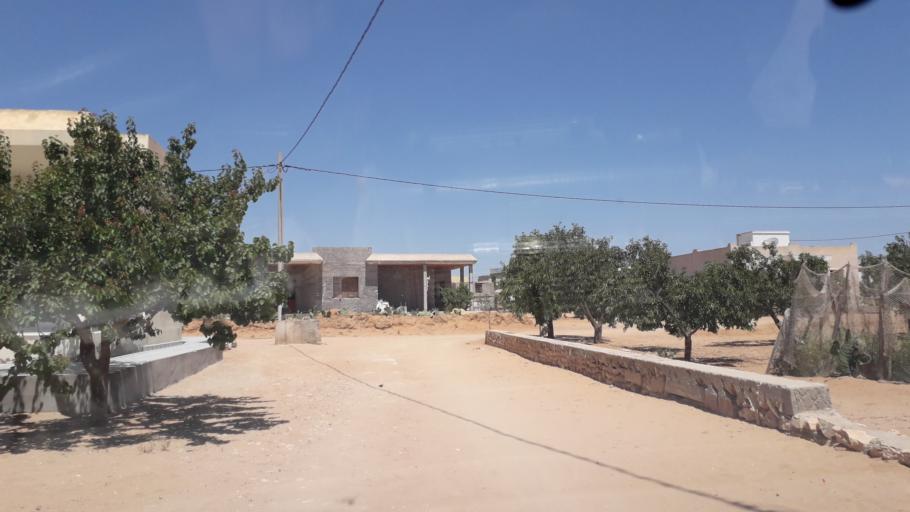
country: TN
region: Safaqis
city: Al Qarmadah
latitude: 34.8303
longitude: 10.7730
